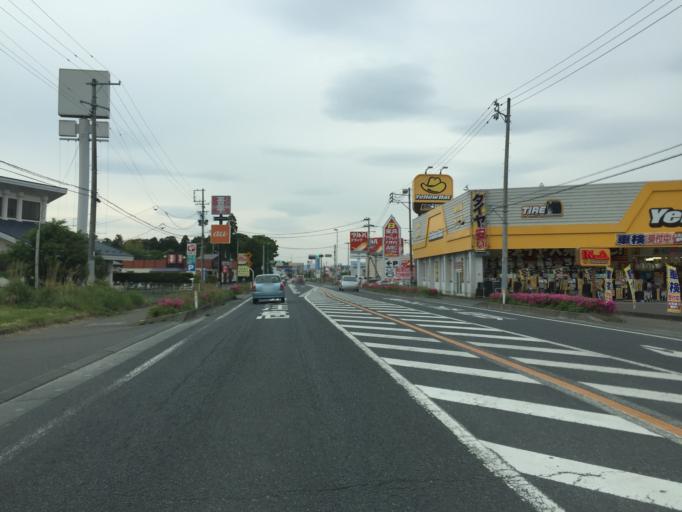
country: JP
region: Miyagi
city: Marumori
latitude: 37.7885
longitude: 140.9316
